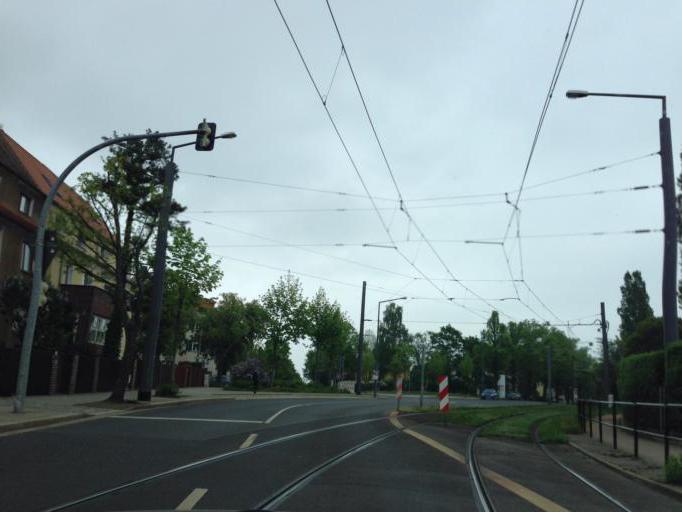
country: DE
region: Saxony
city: Bannewitz
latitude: 51.0204
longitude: 13.7073
